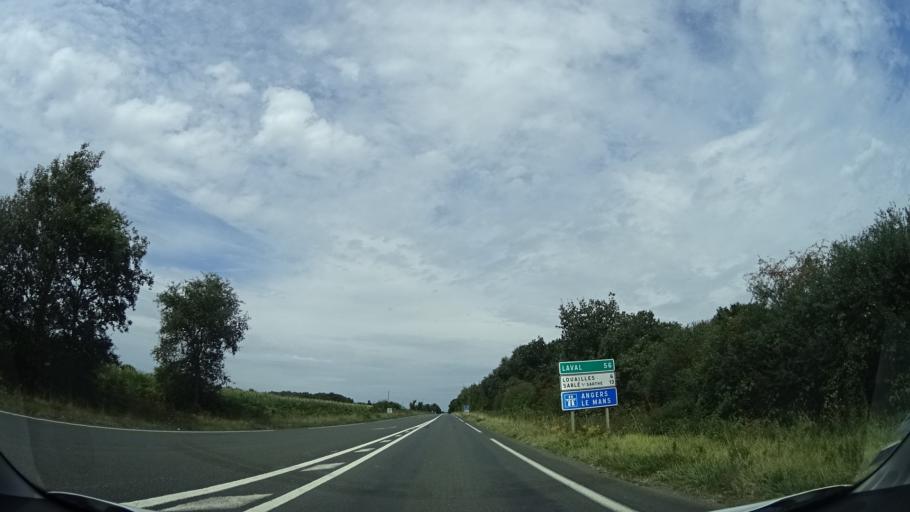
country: FR
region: Pays de la Loire
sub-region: Departement de la Sarthe
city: Vion
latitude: 47.7662
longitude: -0.1933
